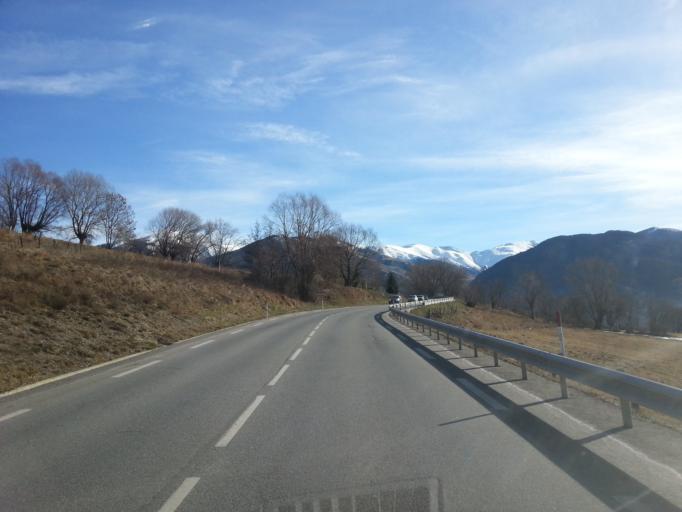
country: ES
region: Catalonia
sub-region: Provincia de Girona
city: Llivia
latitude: 42.4697
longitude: 2.0366
